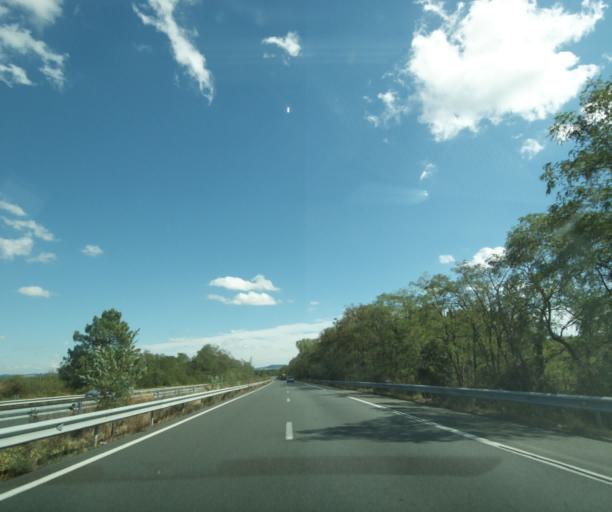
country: FR
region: Aquitaine
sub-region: Departement du Lot-et-Garonne
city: Fourques-sur-Garonne
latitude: 44.3786
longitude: 0.2175
